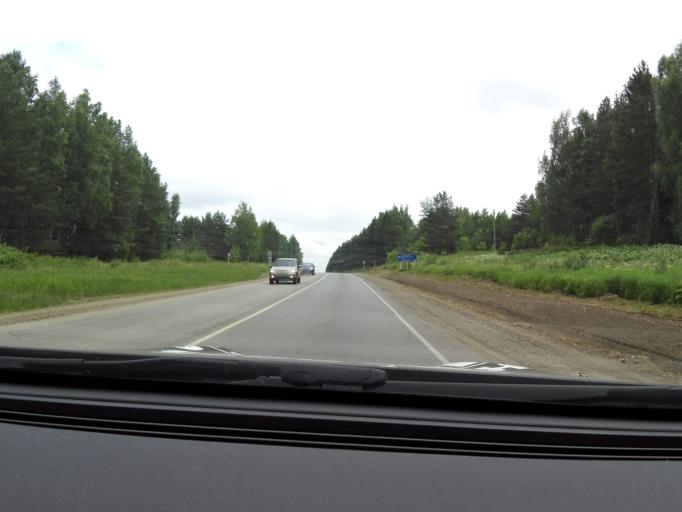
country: RU
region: Perm
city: Kungur
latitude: 57.4778
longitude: 56.7188
